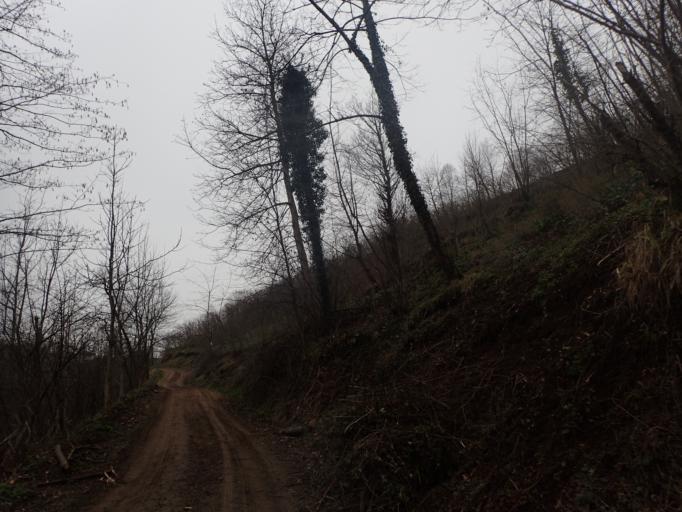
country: TR
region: Ordu
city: Camas
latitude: 40.9189
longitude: 37.5689
